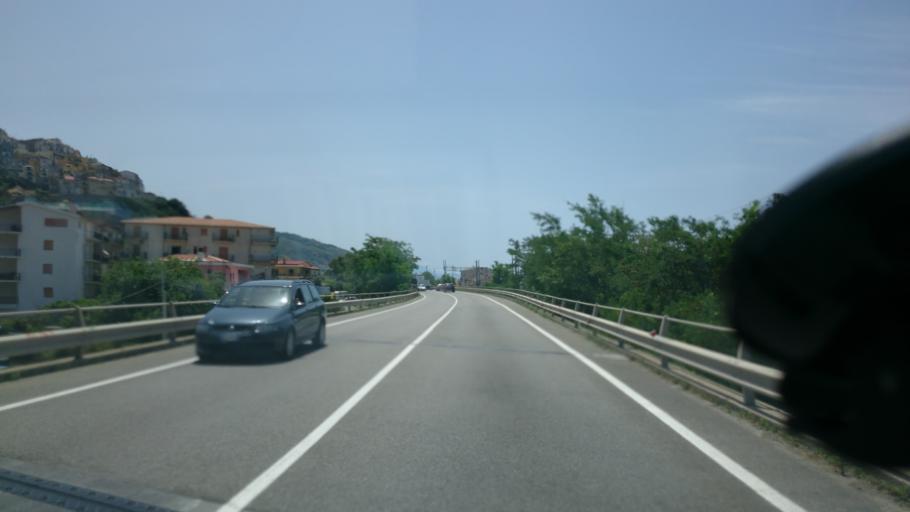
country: IT
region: Calabria
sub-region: Provincia di Cosenza
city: Cetraro Marina
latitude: 39.5213
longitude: 15.9321
